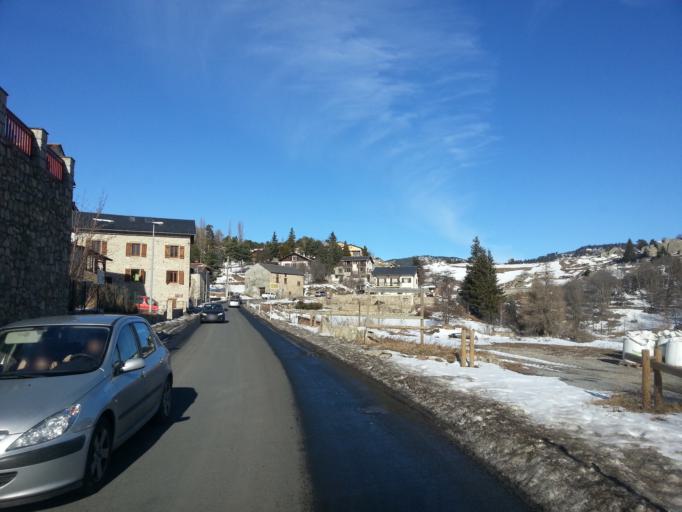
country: ES
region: Catalonia
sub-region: Provincia de Girona
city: Llivia
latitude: 42.5264
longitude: 2.1230
